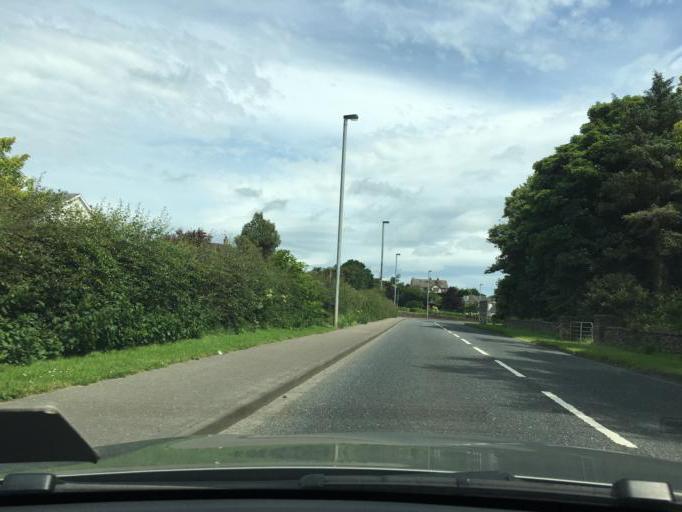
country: GB
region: Northern Ireland
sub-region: City of Derry
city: Derry
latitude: 55.0292
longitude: -7.2973
